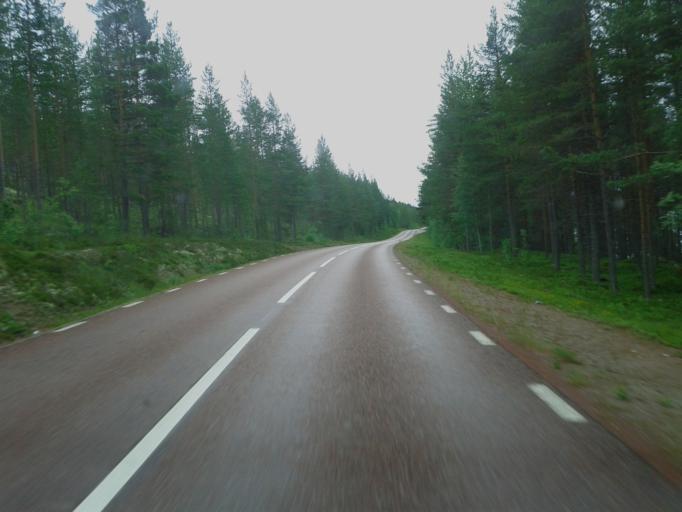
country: NO
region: Hedmark
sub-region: Trysil
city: Innbygda
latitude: 61.7829
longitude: 12.9375
